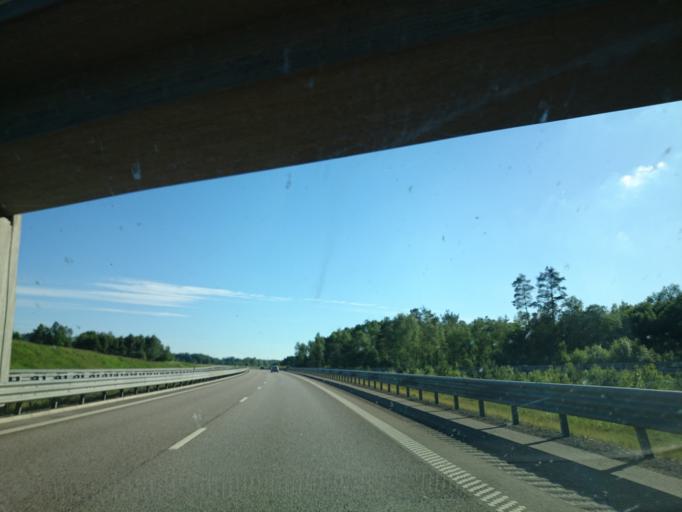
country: SE
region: Skane
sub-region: Orkelljunga Kommun
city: OErkelljunga
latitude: 56.2553
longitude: 13.2109
